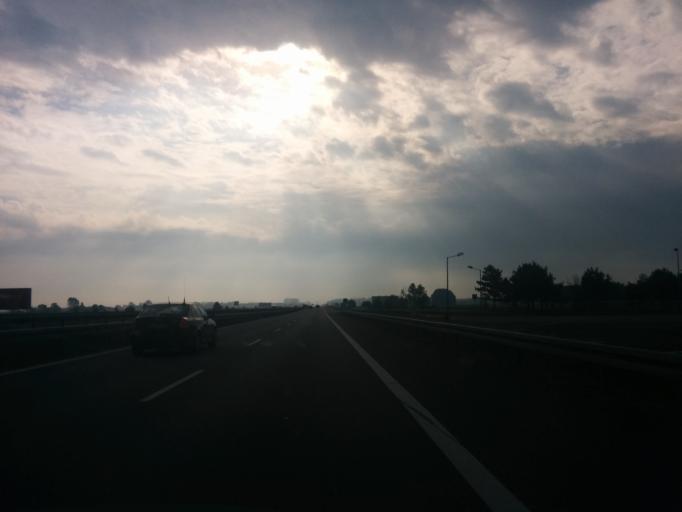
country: PL
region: Masovian Voivodeship
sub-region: Powiat radomski
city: Jedlinsk
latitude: 51.5424
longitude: 21.0600
